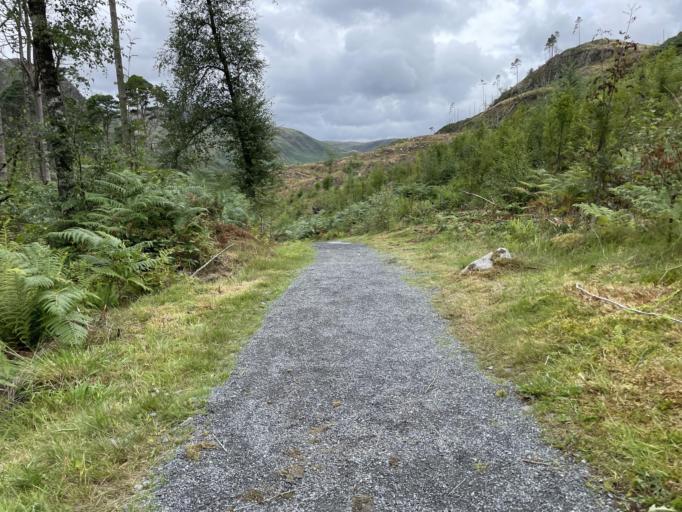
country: GB
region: Scotland
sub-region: Dumfries and Galloway
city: Newton Stewart
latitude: 55.0848
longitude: -4.4965
